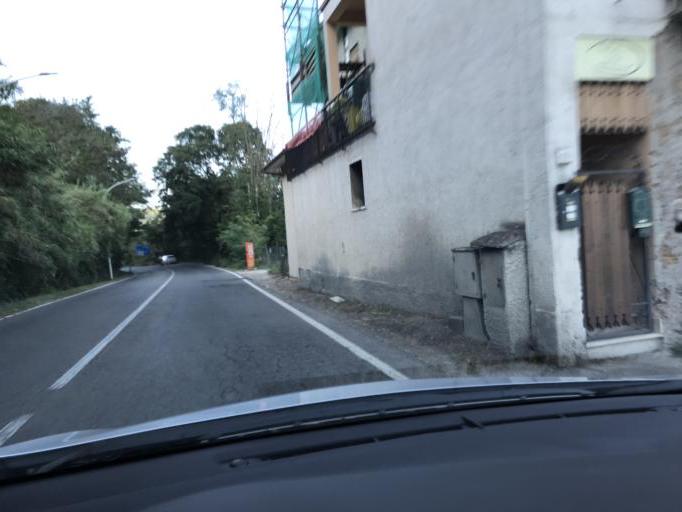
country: IT
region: Latium
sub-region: Provincia di Viterbo
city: Orte
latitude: 42.4598
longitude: 12.3890
